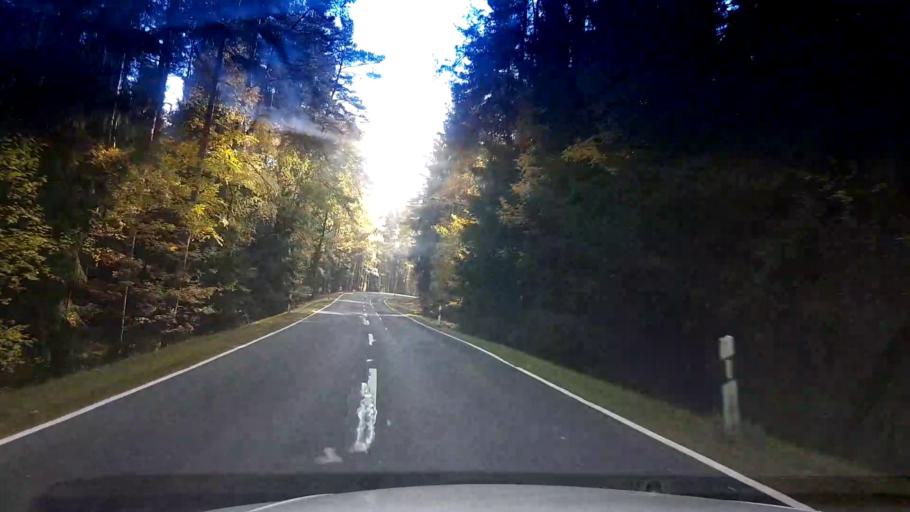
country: DE
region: Bavaria
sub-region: Upper Palatinate
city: Waldsassen
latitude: 50.0292
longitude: 12.3060
